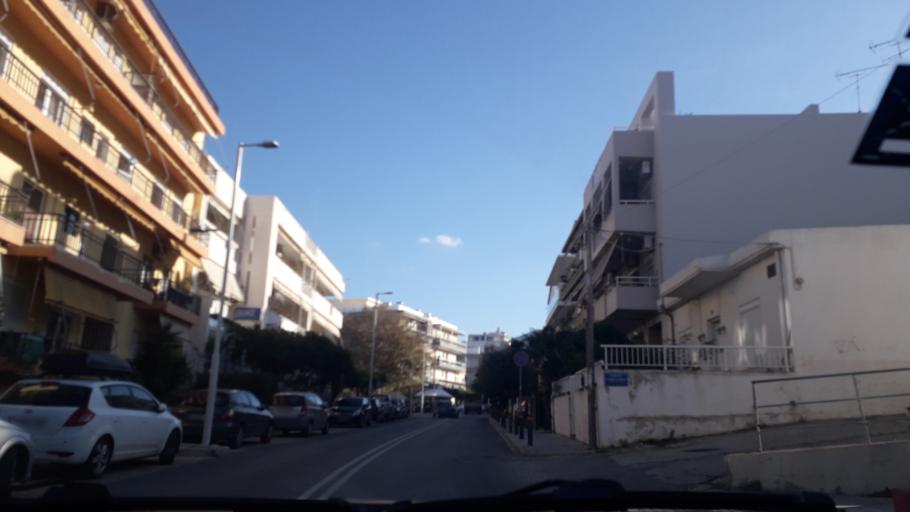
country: GR
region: Crete
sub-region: Nomos Rethymnis
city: Rethymno
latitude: 35.3639
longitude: 24.4715
